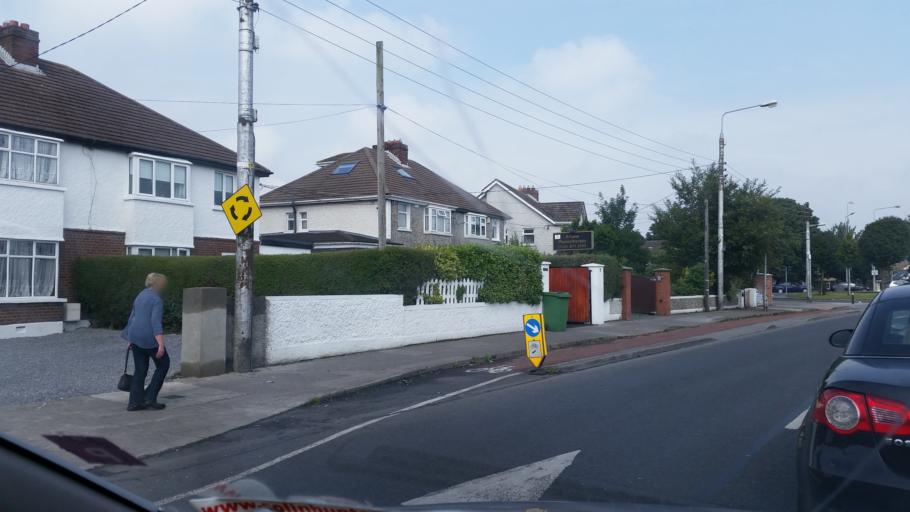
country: IE
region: Leinster
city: Artane
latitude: 53.3826
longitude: -6.2066
